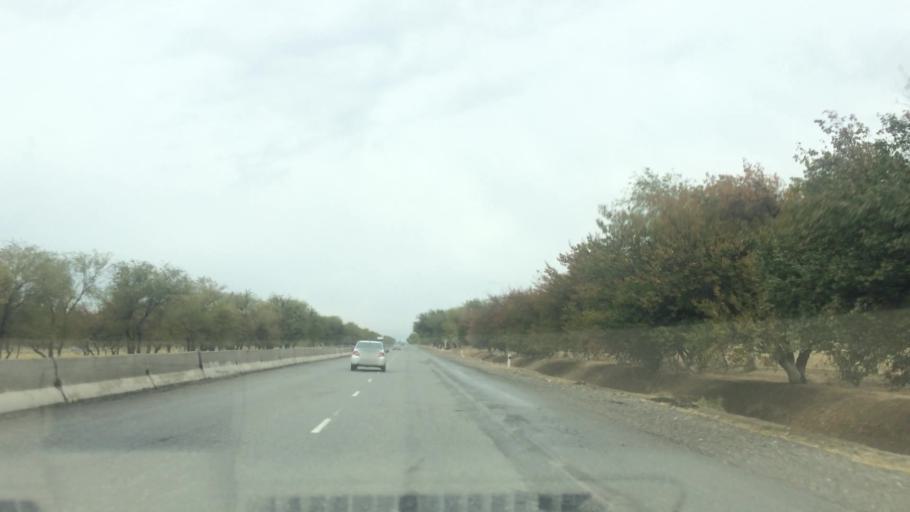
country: UZ
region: Samarqand
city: Bulung'ur
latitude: 39.8114
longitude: 67.3679
